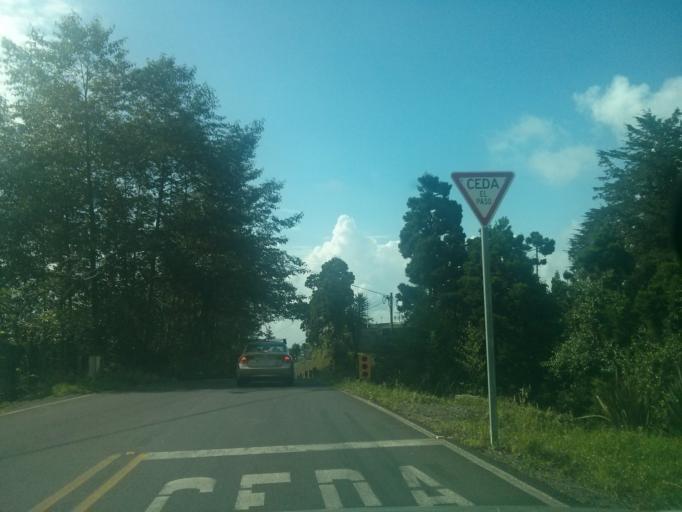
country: CR
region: Alajuela
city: Rio Segundo
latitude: 10.1987
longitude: -84.1583
